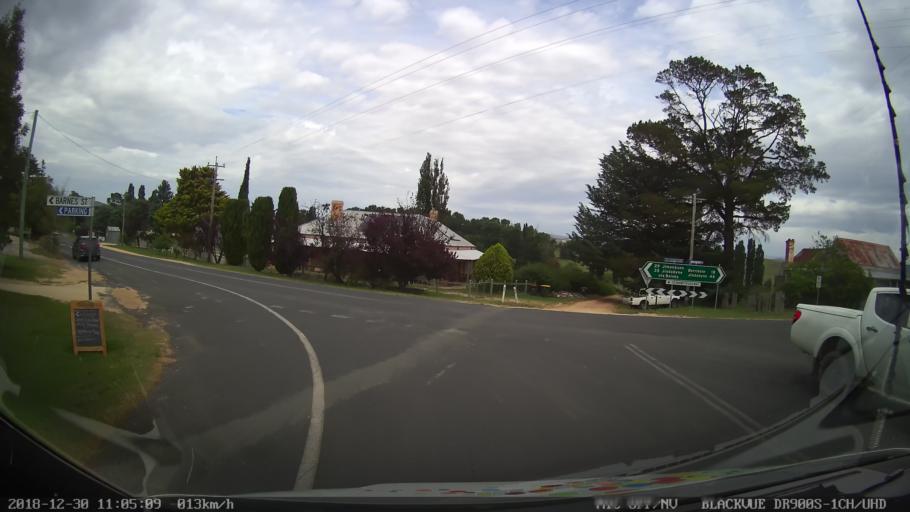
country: AU
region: New South Wales
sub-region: Snowy River
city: Berridale
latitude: -36.5023
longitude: 148.8353
